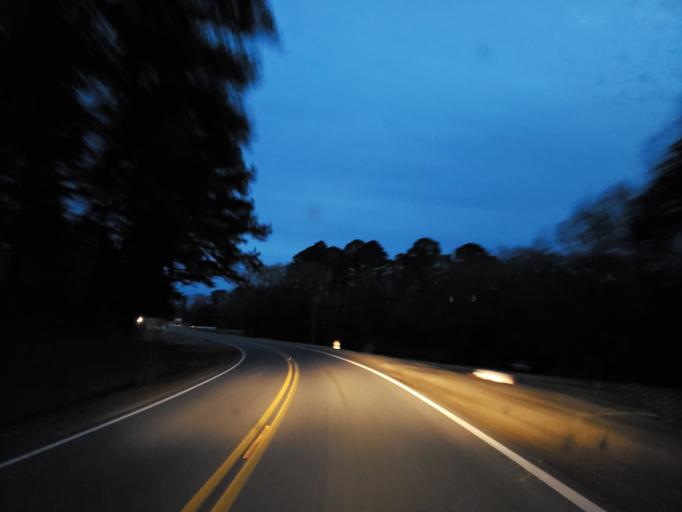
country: US
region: Alabama
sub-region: Greene County
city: Eutaw
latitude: 32.8708
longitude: -87.9276
